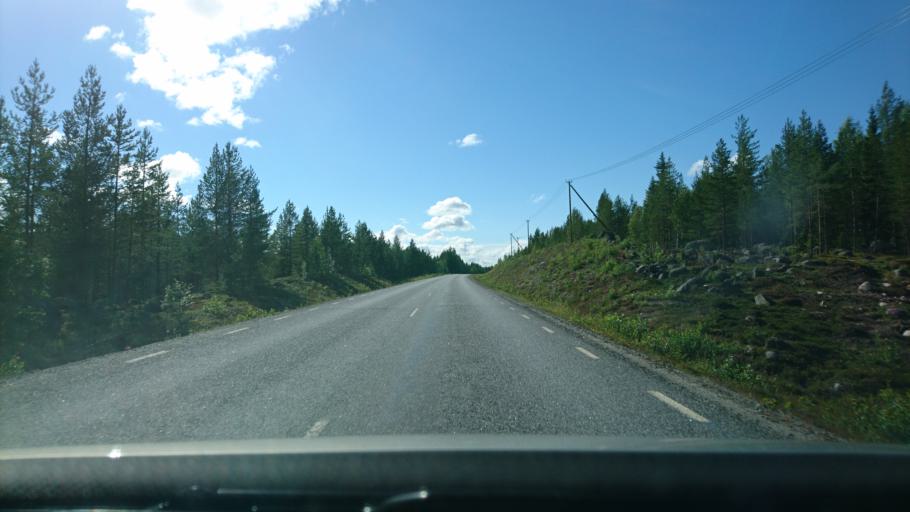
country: SE
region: Vaesterbotten
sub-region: Asele Kommun
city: Asele
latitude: 64.3166
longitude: 17.1379
